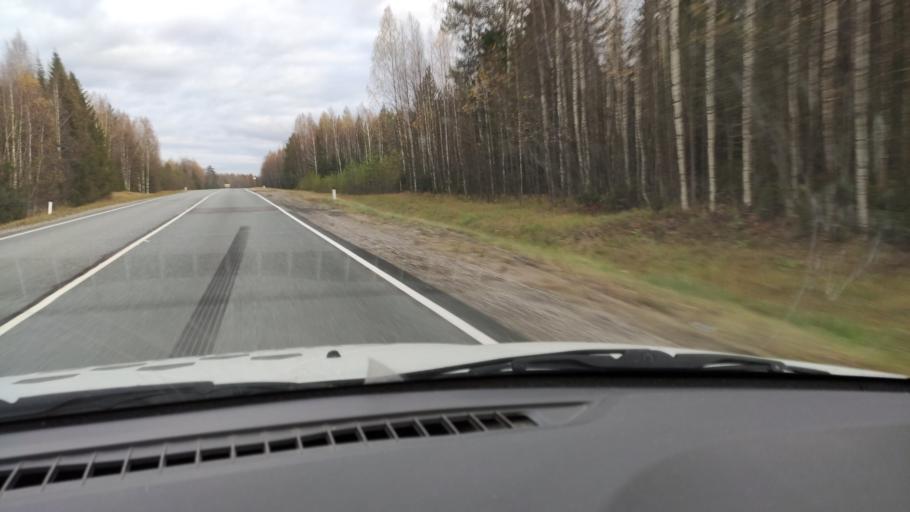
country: RU
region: Kirov
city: Dubrovka
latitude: 58.8989
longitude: 51.3090
